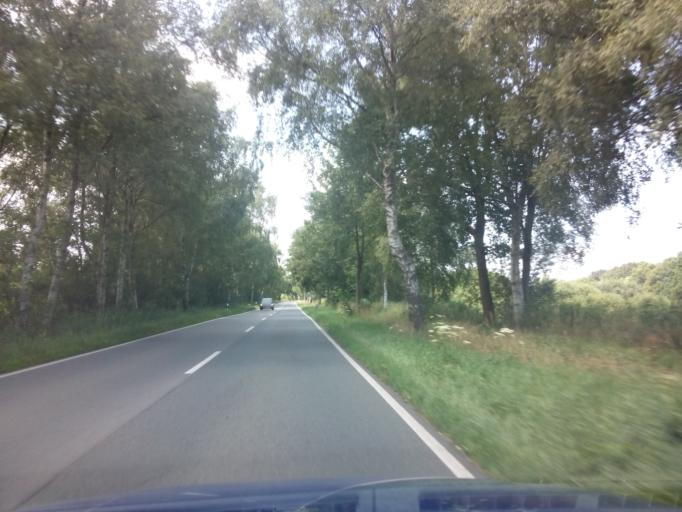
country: DE
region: Lower Saxony
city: Osterholz-Scharmbeck
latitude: 53.2523
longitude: 8.8470
